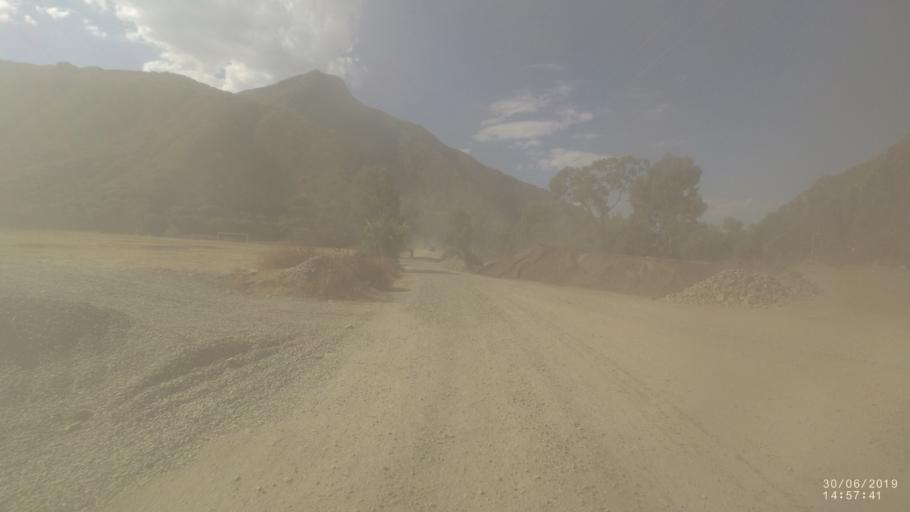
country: BO
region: Cochabamba
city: Irpa Irpa
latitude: -17.7429
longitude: -66.3528
